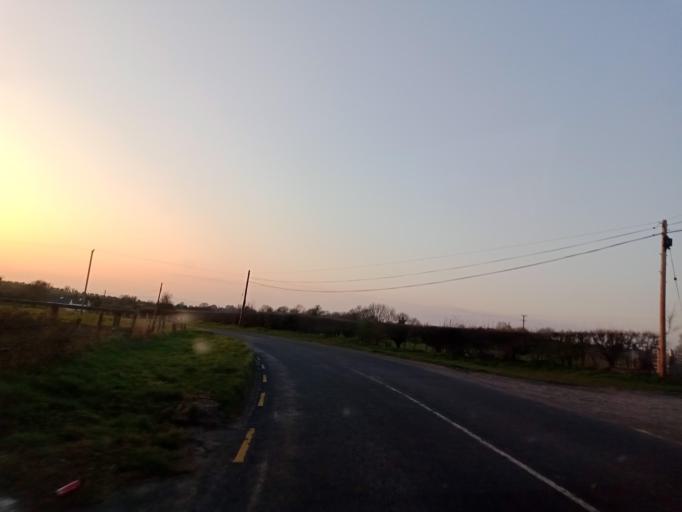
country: IE
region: Leinster
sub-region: Laois
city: Abbeyleix
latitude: 52.8989
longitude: -7.3187
